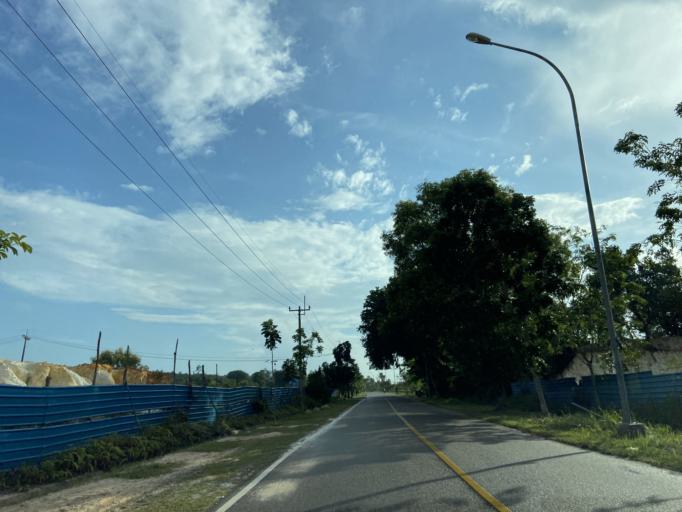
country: SG
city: Singapore
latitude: 0.9571
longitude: 104.0532
